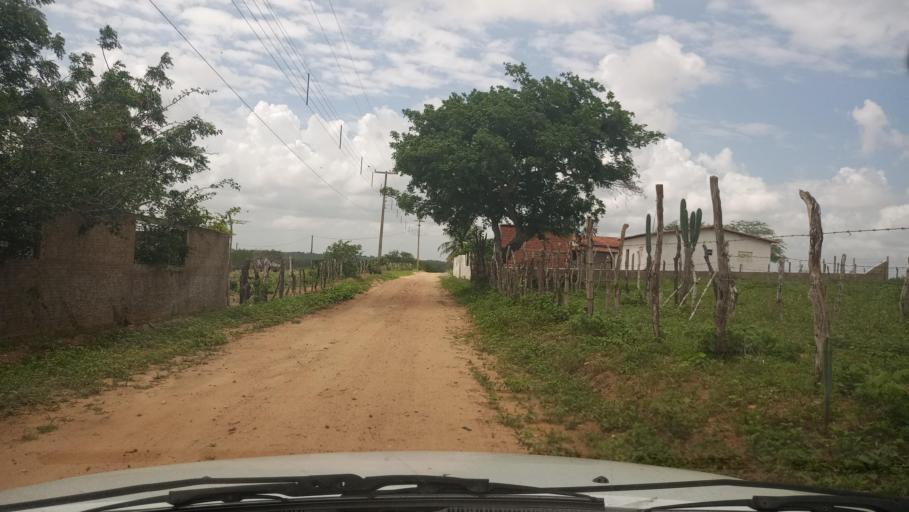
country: BR
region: Rio Grande do Norte
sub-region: Sao Paulo Do Potengi
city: Sao Paulo do Potengi
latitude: -5.9177
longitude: -35.6944
